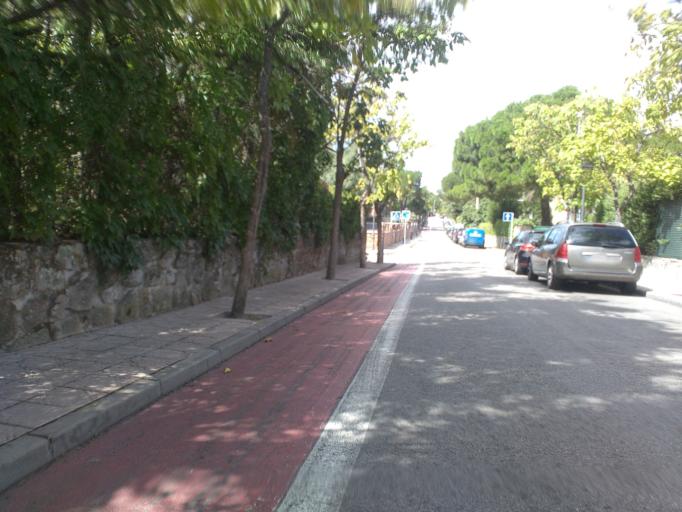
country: ES
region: Madrid
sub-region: Provincia de Madrid
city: Torrelodones
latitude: 40.5793
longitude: -3.9528
